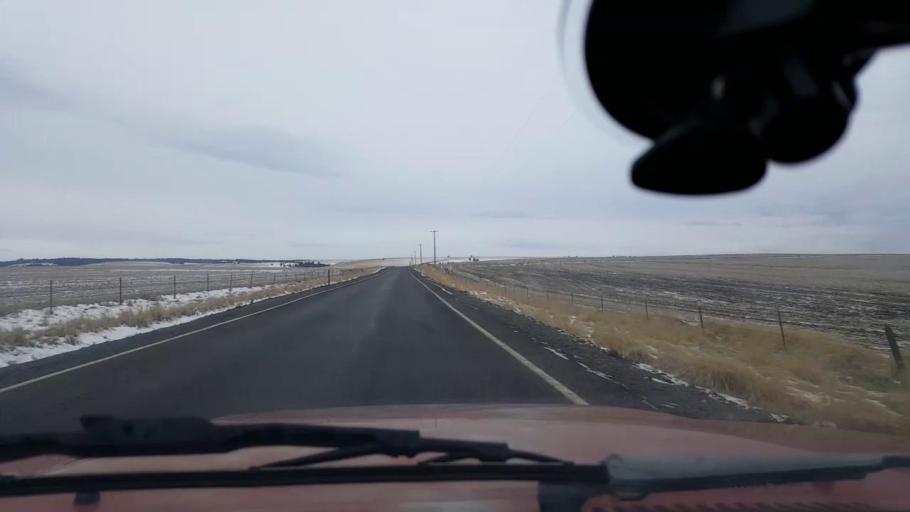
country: US
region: Washington
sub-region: Garfield County
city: Pomeroy
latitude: 46.3216
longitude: -117.3803
